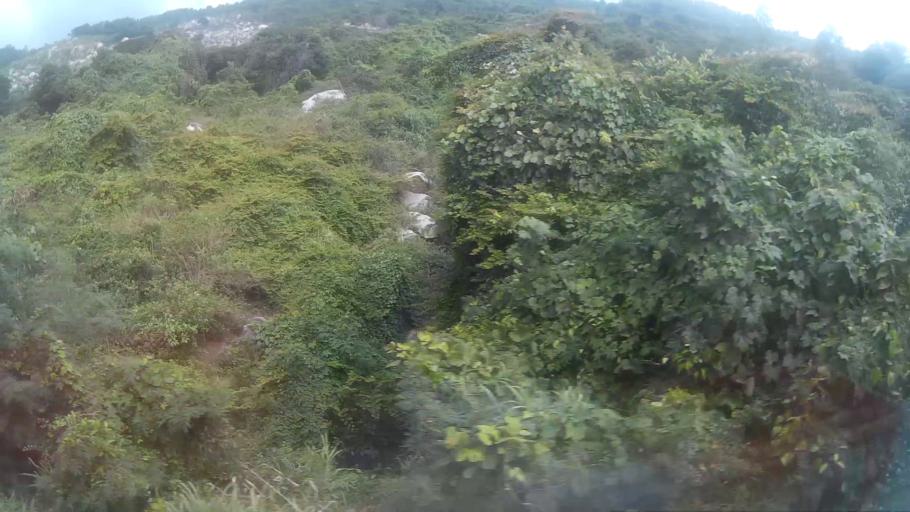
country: VN
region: Khanh Hoa
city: Van Gia
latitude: 12.8398
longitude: 109.3810
